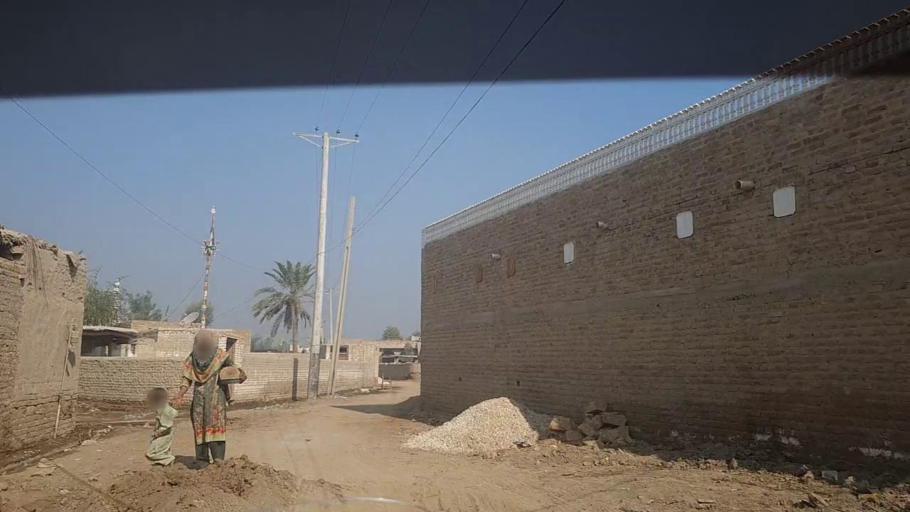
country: PK
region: Sindh
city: Khairpur
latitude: 27.4691
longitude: 68.7131
